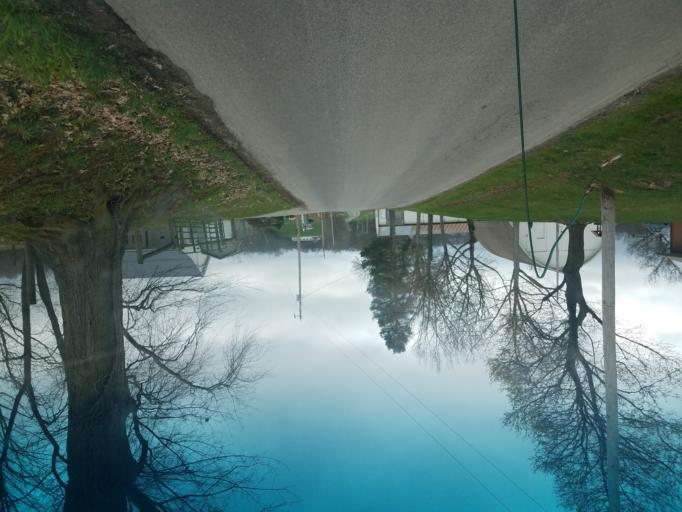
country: US
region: Ohio
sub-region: Stark County
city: Beach City
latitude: 40.6358
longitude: -81.6781
